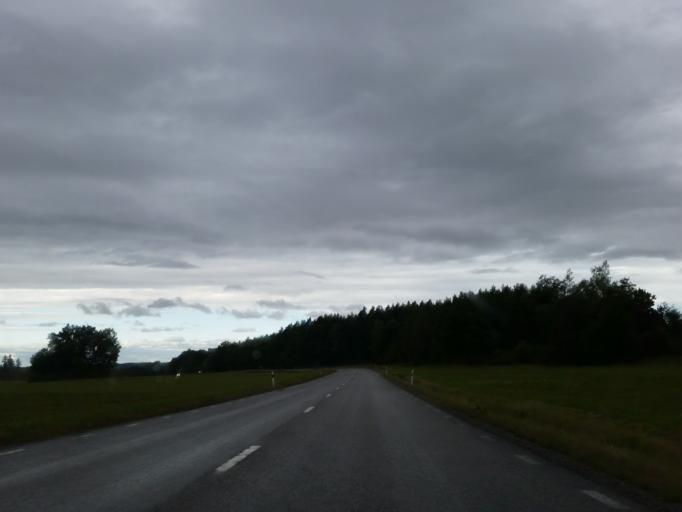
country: SE
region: Uppsala
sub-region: Habo Kommun
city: Balsta
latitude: 59.6482
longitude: 17.4259
